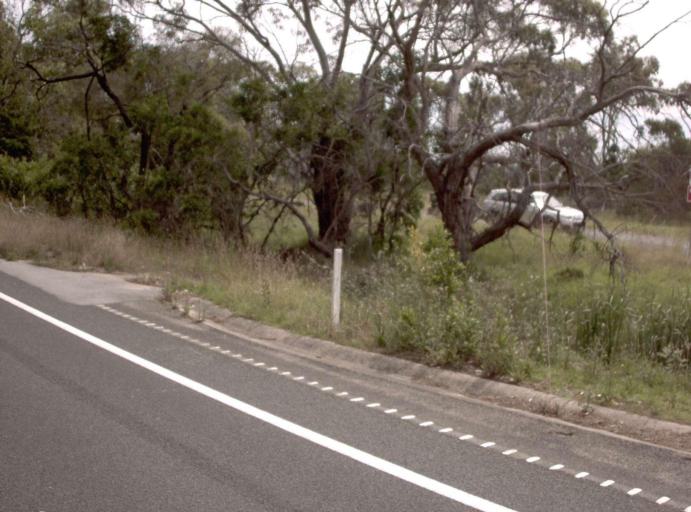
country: AU
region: Victoria
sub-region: Mornington Peninsula
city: Mount Martha
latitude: -38.2655
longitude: 145.0731
